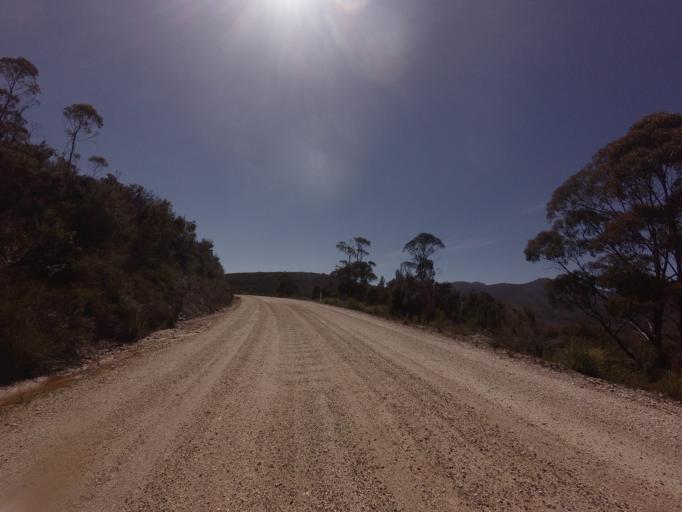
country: AU
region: Tasmania
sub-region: Huon Valley
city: Geeveston
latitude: -43.0367
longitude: 146.3327
